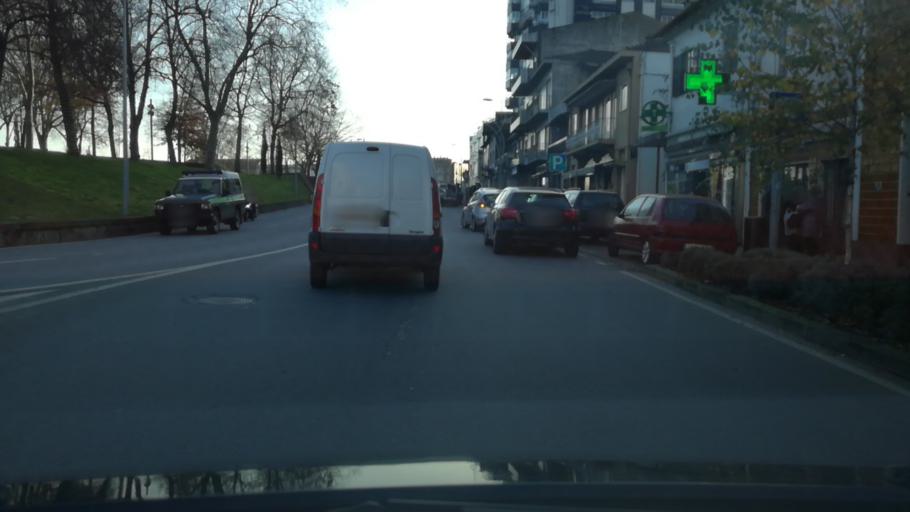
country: PT
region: Porto
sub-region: Trofa
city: Bougado
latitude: 41.3371
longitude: -8.5598
